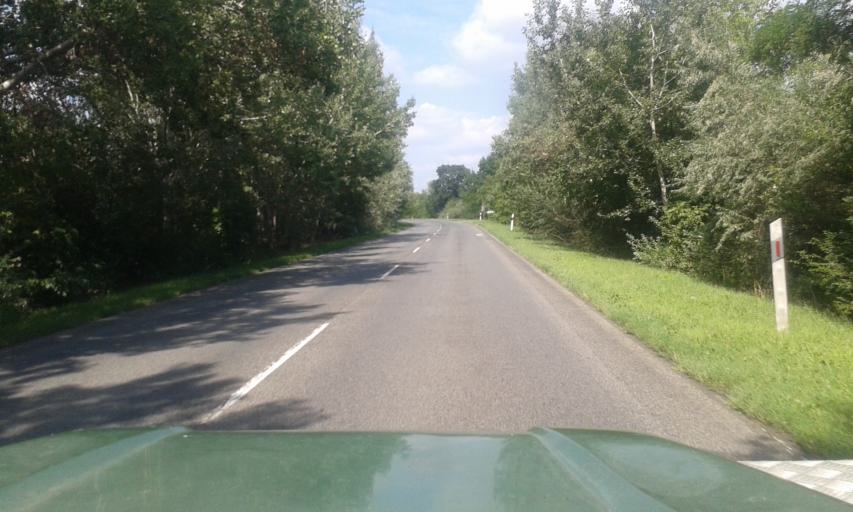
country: HU
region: Csongrad
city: Szatymaz
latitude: 46.3400
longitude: 20.0657
